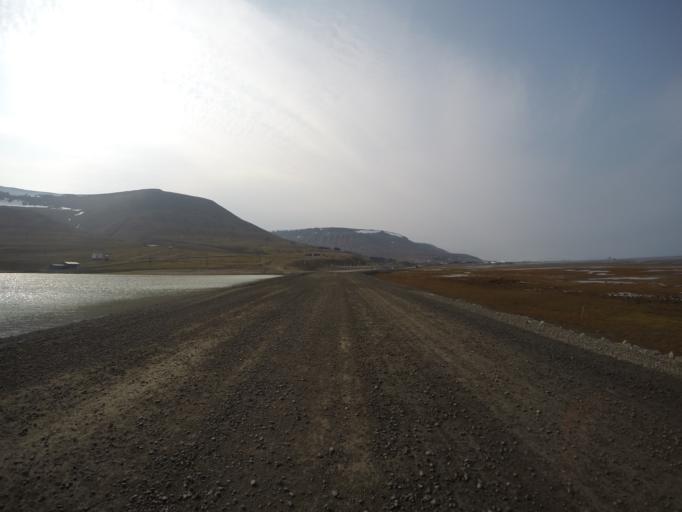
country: SJ
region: Svalbard
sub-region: Spitsbergen
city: Longyearbyen
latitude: 78.2181
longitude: 15.7047
